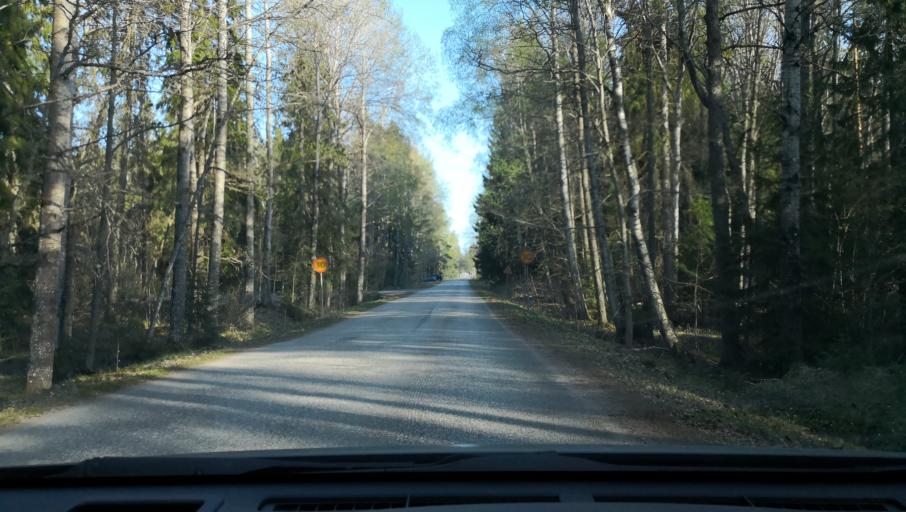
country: SE
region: Uppsala
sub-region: Heby Kommun
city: Tarnsjo
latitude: 60.2715
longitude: 16.9059
